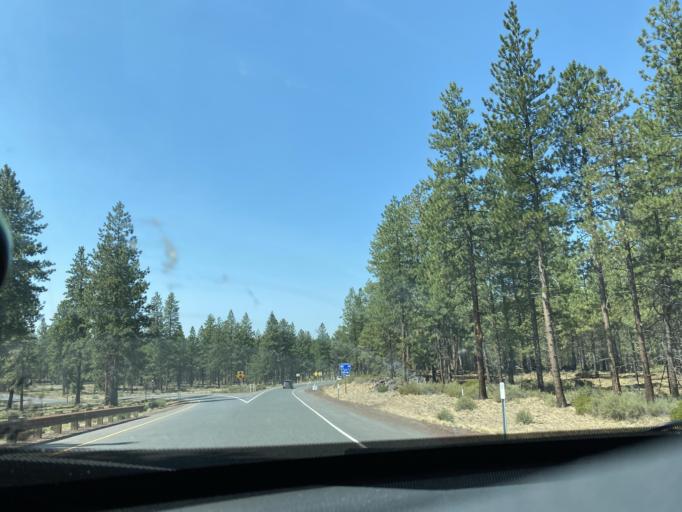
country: US
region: Oregon
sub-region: Deschutes County
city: Sunriver
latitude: 43.8910
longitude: -121.3803
